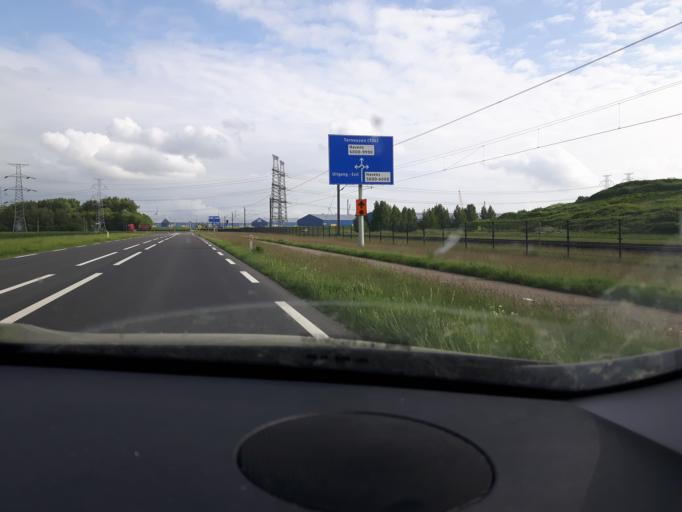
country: NL
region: Zeeland
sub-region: Gemeente Borsele
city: Borssele
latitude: 51.4657
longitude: 3.7274
